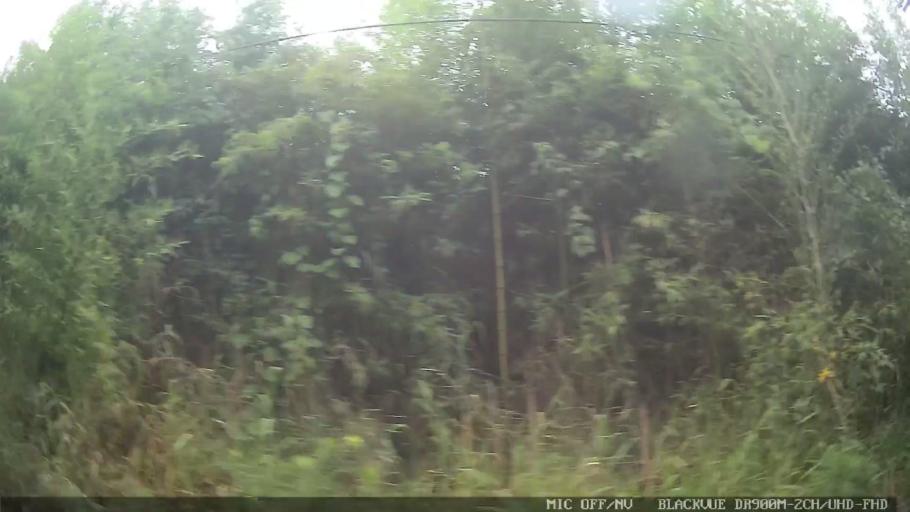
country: BR
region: Sao Paulo
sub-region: Suzano
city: Suzano
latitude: -23.6295
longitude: -46.2904
